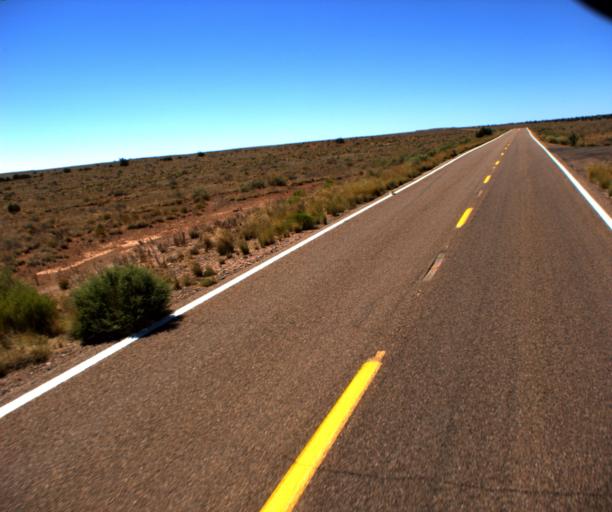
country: US
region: Arizona
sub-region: Navajo County
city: Winslow
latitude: 34.9479
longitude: -110.6458
